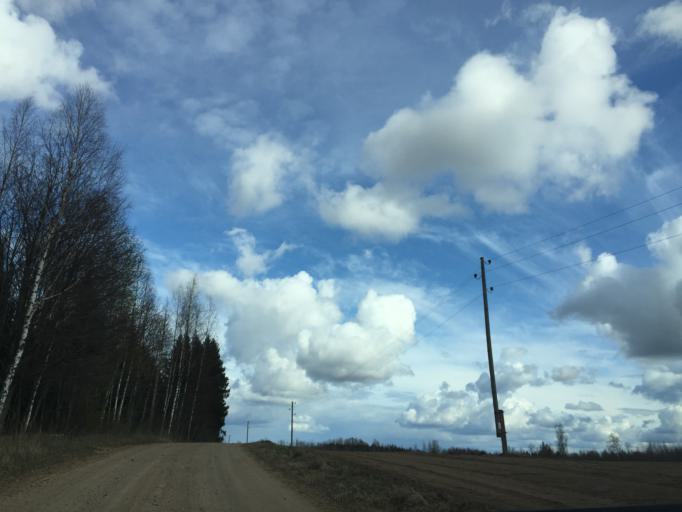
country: LV
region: Burtnieki
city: Matisi
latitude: 57.6139
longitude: 25.0095
